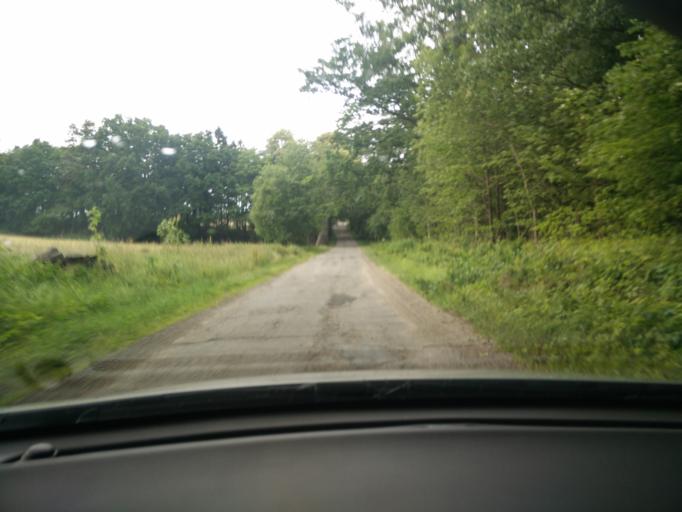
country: PL
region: Pomeranian Voivodeship
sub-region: Powiat pucki
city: Mrzezino
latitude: 54.6781
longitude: 18.4596
